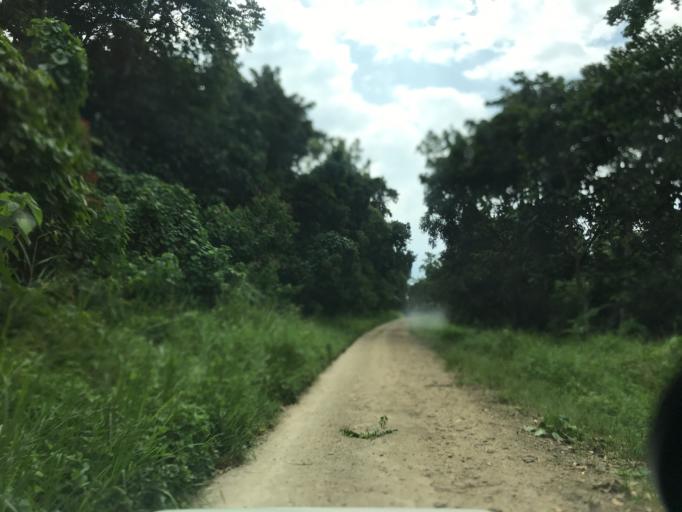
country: VU
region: Sanma
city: Port-Olry
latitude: -15.1721
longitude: 166.9509
